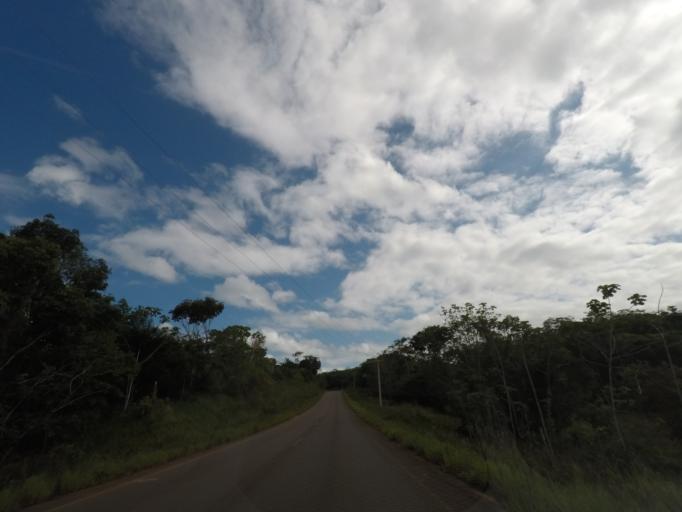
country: BR
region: Bahia
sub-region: Itacare
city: Itacare
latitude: -14.2222
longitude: -39.0979
